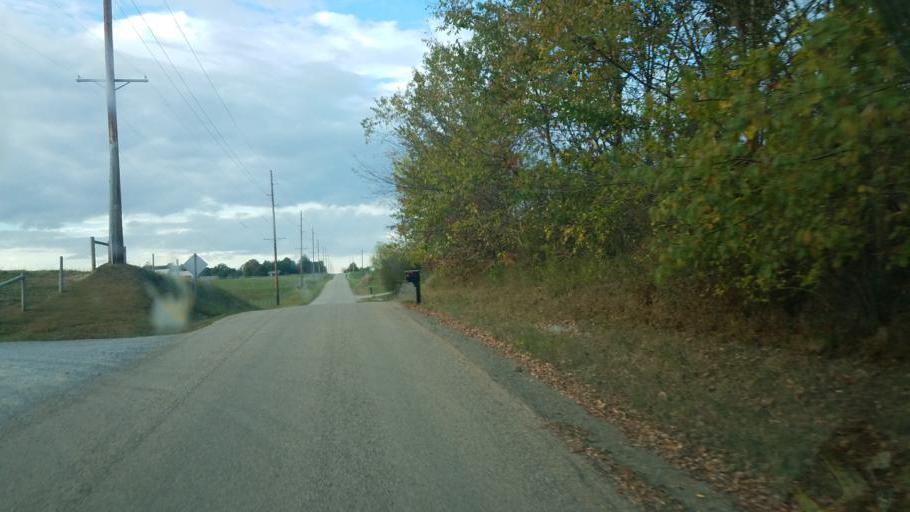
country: US
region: Ohio
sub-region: Ashland County
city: Loudonville
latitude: 40.6876
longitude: -82.2123
